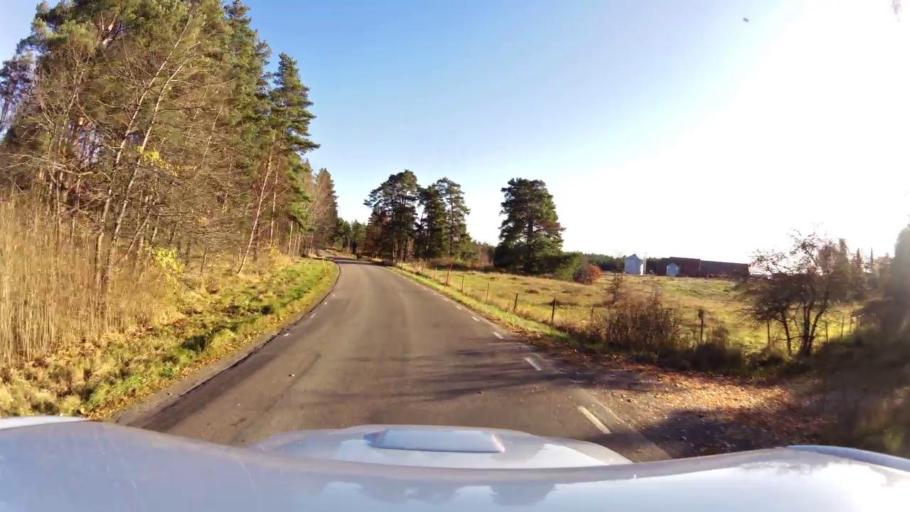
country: SE
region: OEstergoetland
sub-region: Linkopings Kommun
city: Linkoping
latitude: 58.3512
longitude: 15.5943
